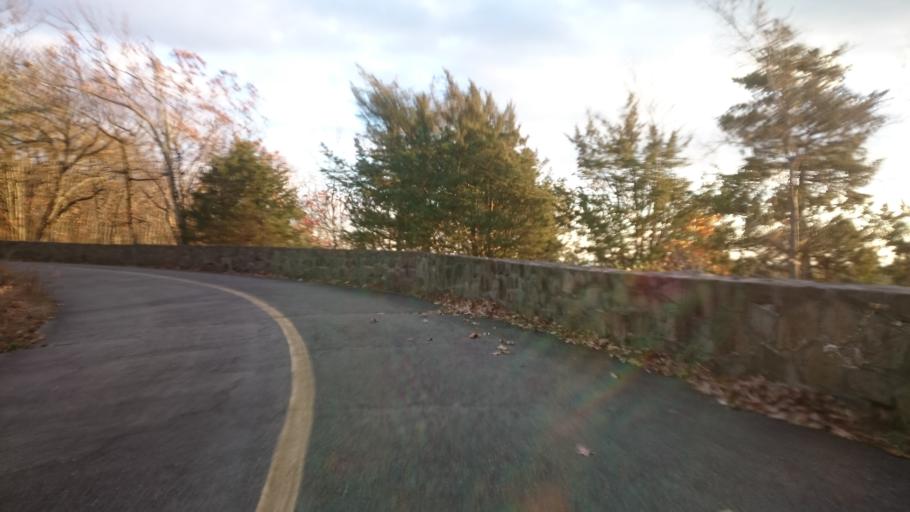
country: US
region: Connecticut
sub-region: New Haven County
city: New Haven
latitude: 41.3343
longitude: -72.9648
